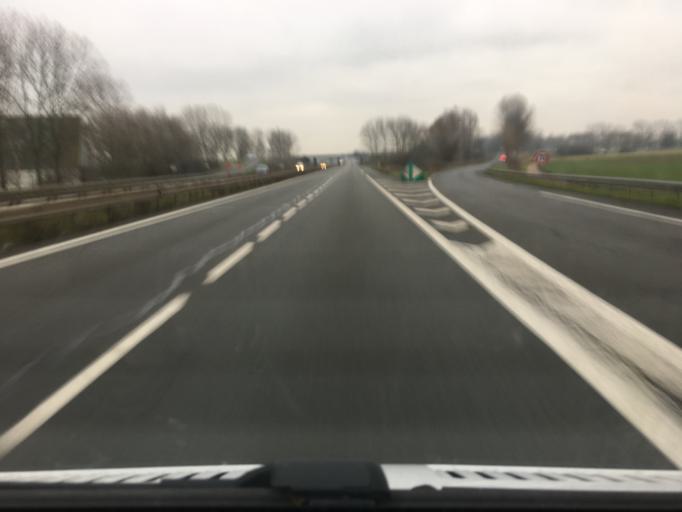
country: FR
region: Nord-Pas-de-Calais
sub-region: Departement du Nord
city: Socx
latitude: 50.9499
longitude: 2.4267
